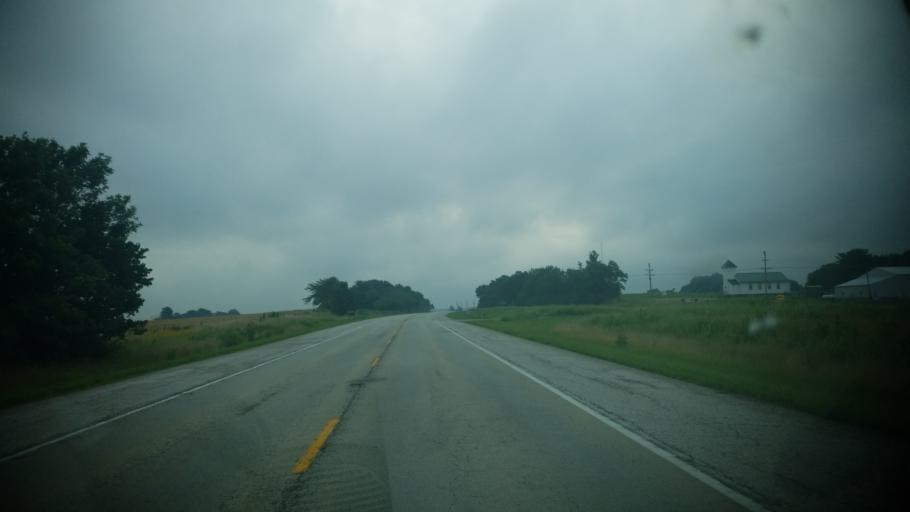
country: US
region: Illinois
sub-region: Clay County
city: Flora
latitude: 38.6775
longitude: -88.3986
